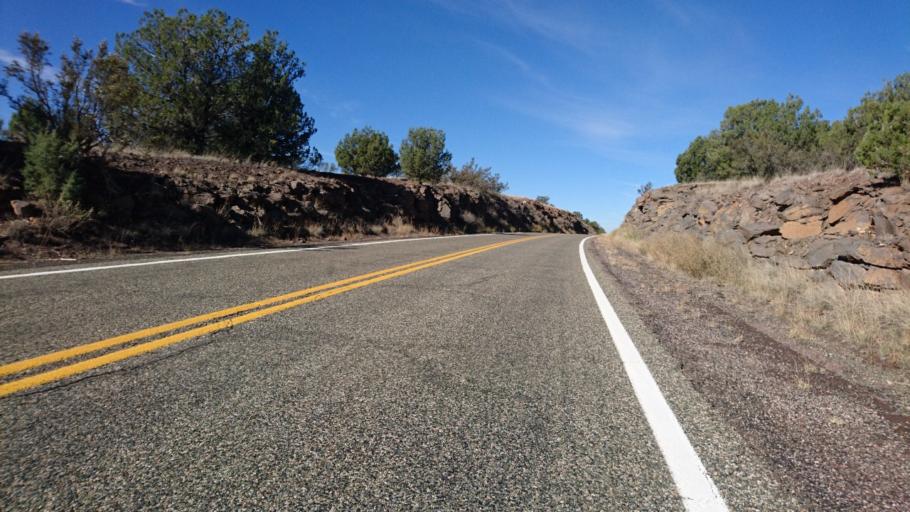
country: US
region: Arizona
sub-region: Yavapai County
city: Paulden
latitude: 35.2797
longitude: -112.7026
